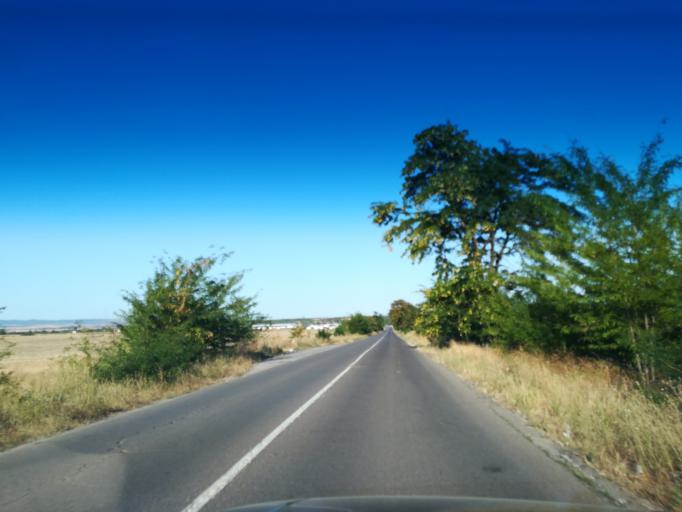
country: BG
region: Stara Zagora
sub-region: Obshtina Chirpan
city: Chirpan
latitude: 42.1742
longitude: 25.1967
